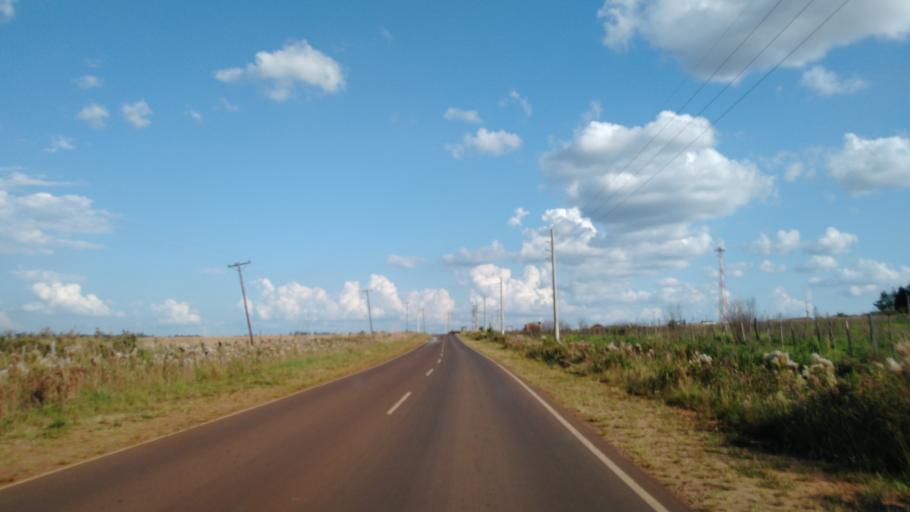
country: PY
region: Itapua
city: San Juan del Parana
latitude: -27.3880
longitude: -55.9912
